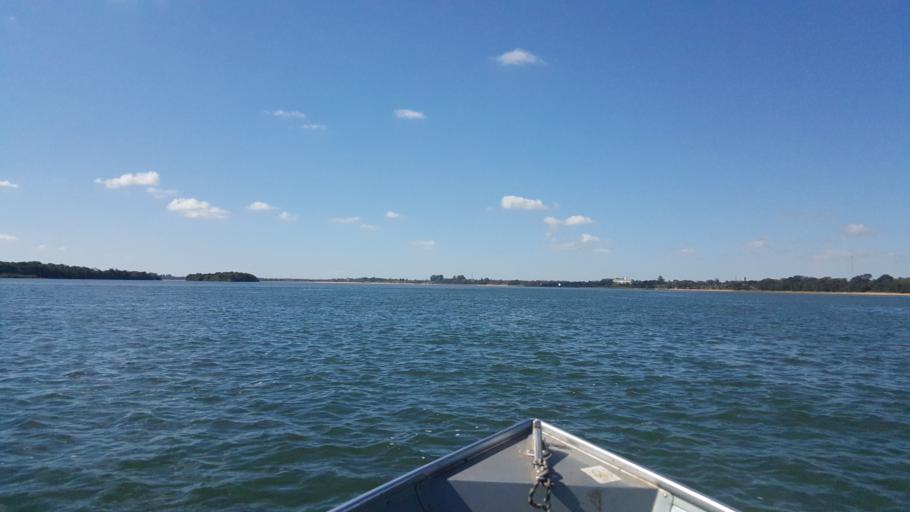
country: AR
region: Corrientes
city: Ituzaingo
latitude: -27.5812
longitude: -56.7003
